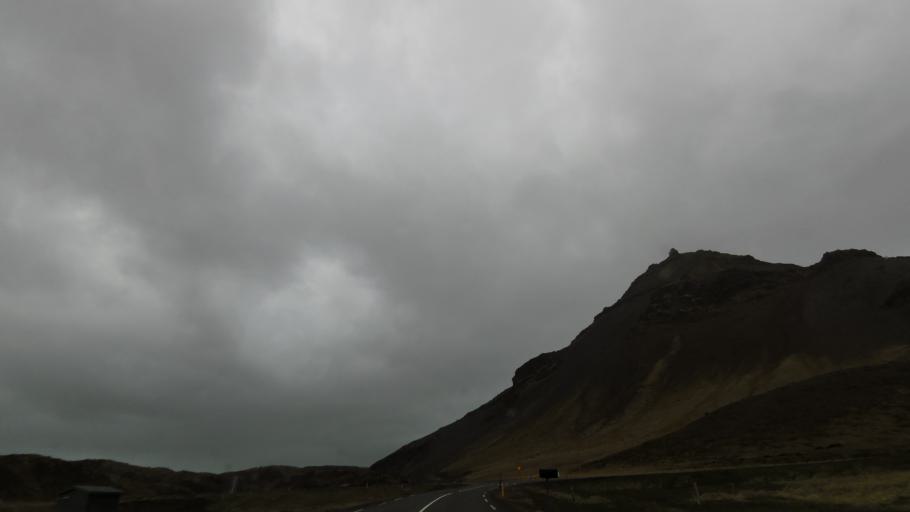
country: IS
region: West
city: Olafsvik
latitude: 64.7670
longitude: -23.6418
